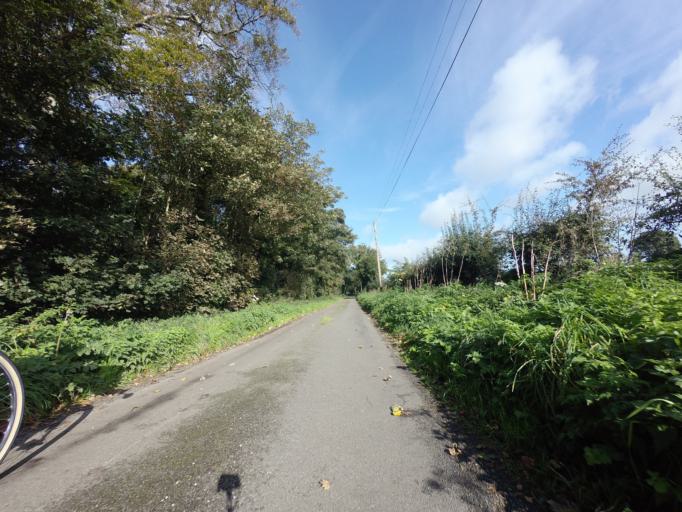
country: GB
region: England
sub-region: Norfolk
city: Fakenham
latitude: 52.8881
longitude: 0.6837
